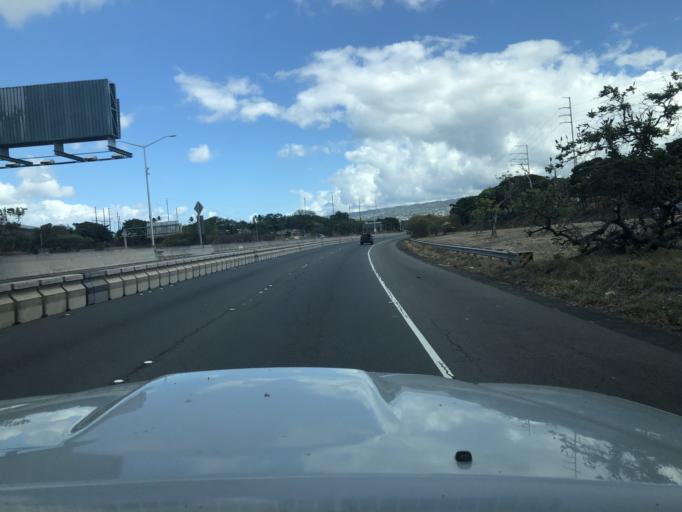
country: US
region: Hawaii
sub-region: Honolulu County
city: Hickam Field
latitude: 21.3468
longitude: -157.9334
